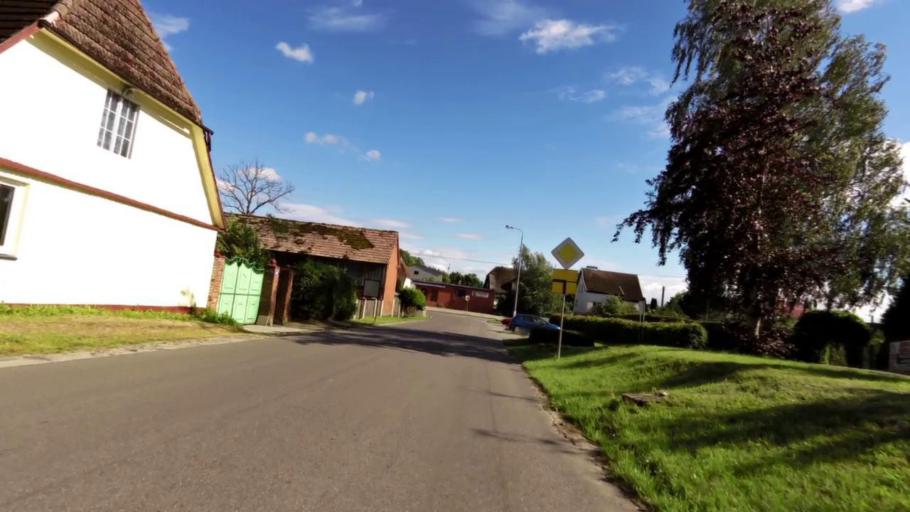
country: PL
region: West Pomeranian Voivodeship
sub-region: Powiat slawienski
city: Slawno
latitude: 54.4351
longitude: 16.7333
